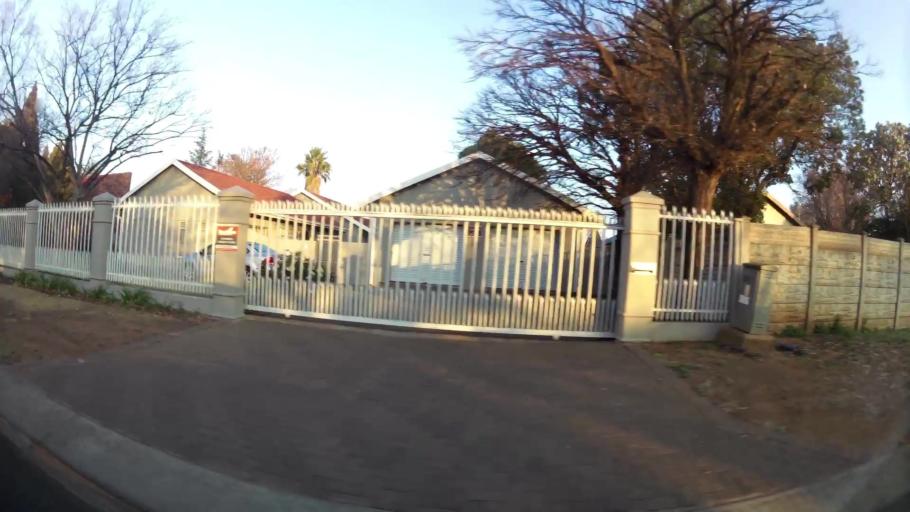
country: ZA
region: Orange Free State
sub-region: Mangaung Metropolitan Municipality
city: Bloemfontein
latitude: -29.1067
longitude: 26.1544
